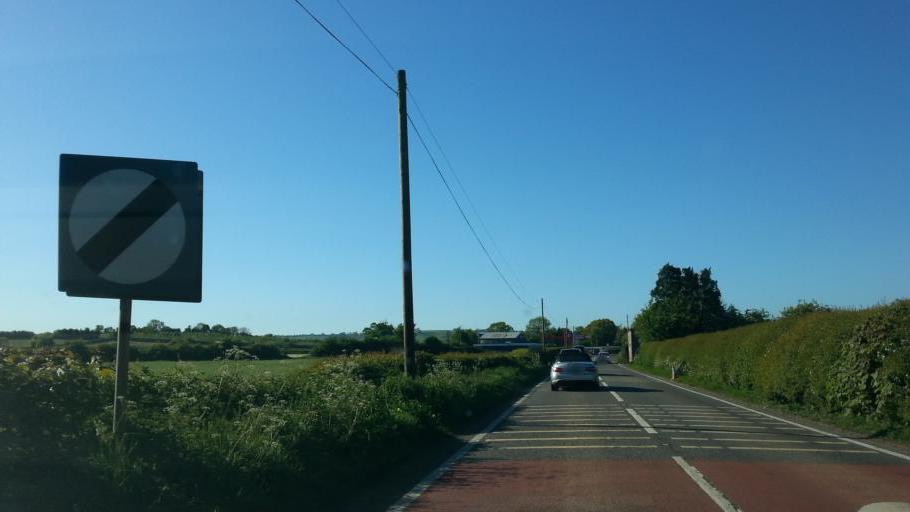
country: GB
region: England
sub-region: Somerset
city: Castle Cary
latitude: 51.1015
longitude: -2.5229
